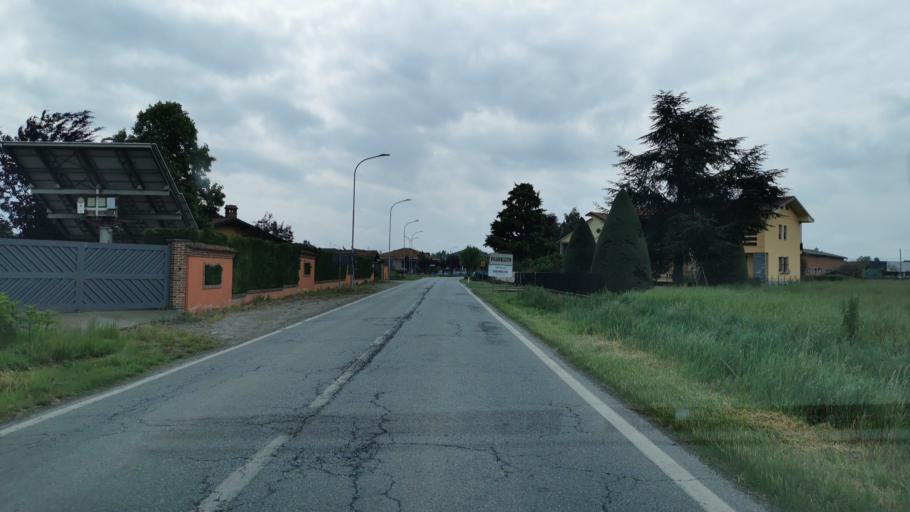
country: IT
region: Piedmont
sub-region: Provincia di Cuneo
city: Villafalletto
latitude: 44.5543
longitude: 7.5376
